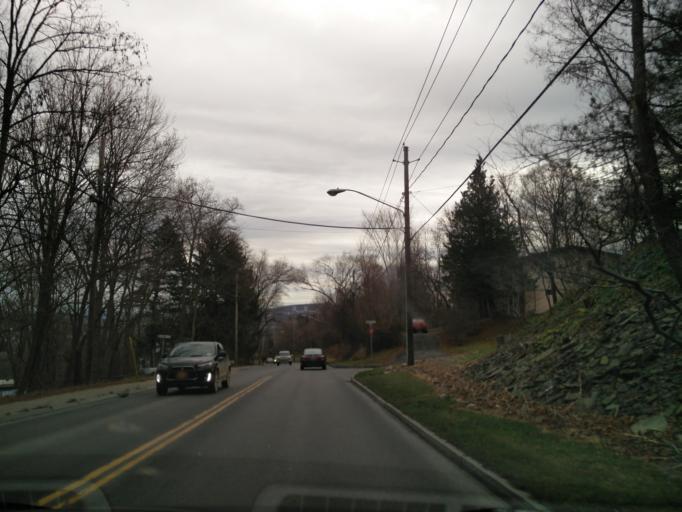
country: US
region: New York
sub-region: Tompkins County
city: Northwest Ithaca
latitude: 42.4549
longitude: -76.5217
